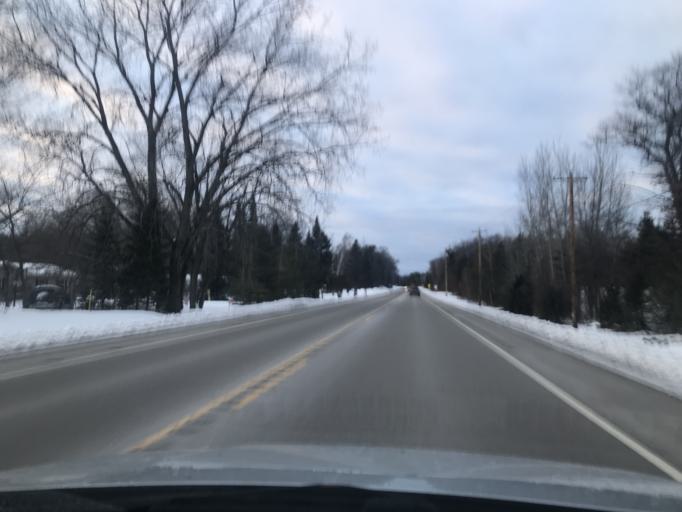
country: US
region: Wisconsin
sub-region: Marinette County
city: Peshtigo
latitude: 45.1628
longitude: -87.7250
